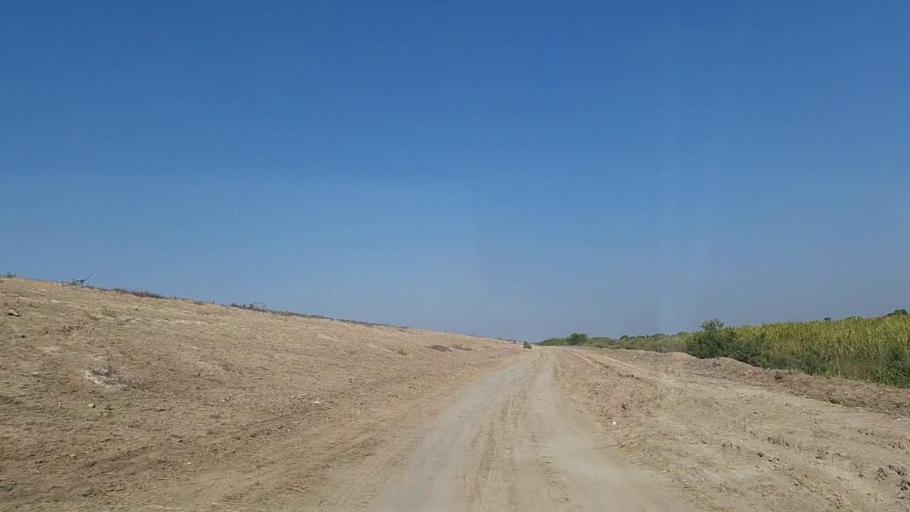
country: PK
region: Sindh
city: Chuhar Jamali
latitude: 24.4684
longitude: 68.0063
